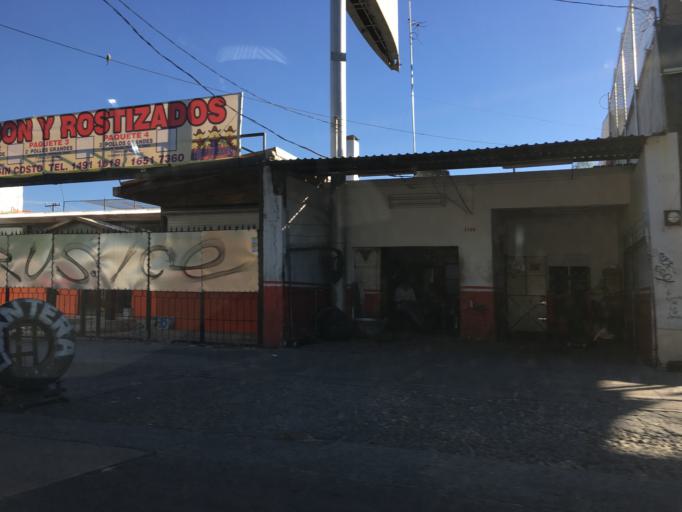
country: MX
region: Jalisco
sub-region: Zapopan
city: Zapopan
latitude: 20.7064
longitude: -103.3504
